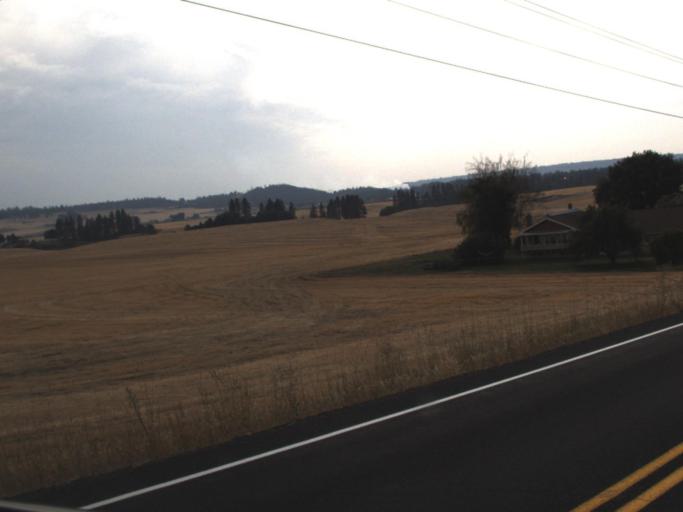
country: US
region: Washington
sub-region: Spokane County
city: Mead
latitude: 47.7875
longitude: -117.2917
